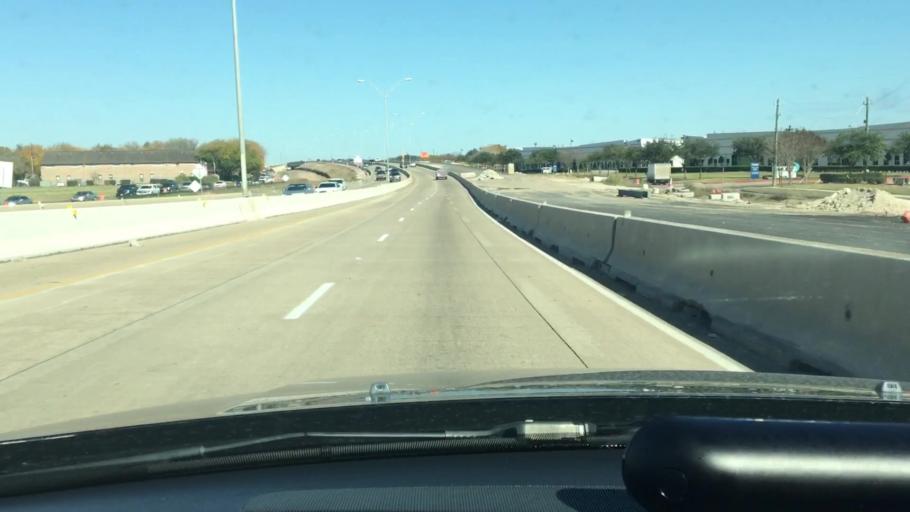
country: US
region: Texas
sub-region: Harris County
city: Deer Park
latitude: 29.6852
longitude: -95.1541
